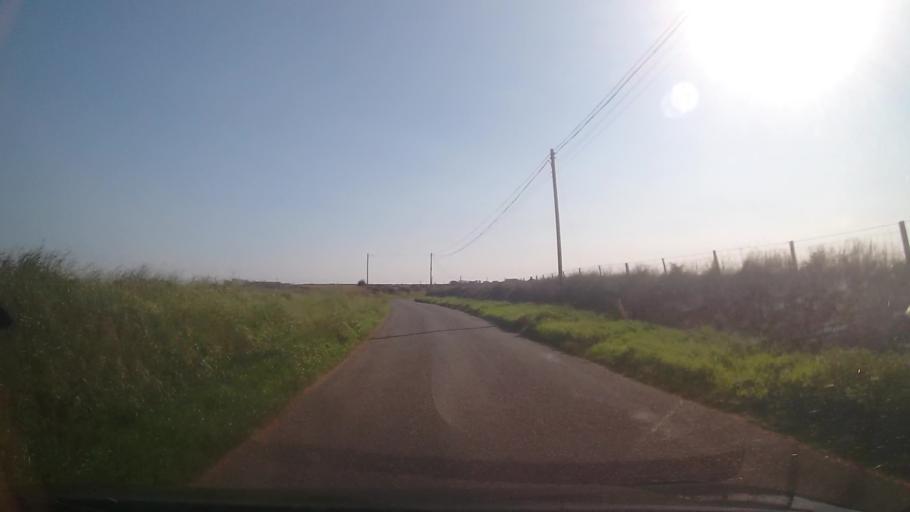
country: GB
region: Wales
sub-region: Pembrokeshire
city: Saint David's
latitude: 51.8958
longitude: -5.2486
